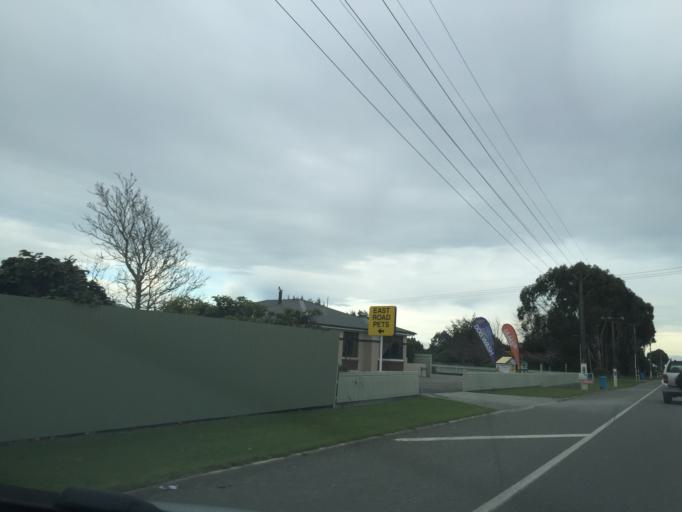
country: NZ
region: Southland
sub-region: Invercargill City
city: Invercargill
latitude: -46.4033
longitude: 168.4017
